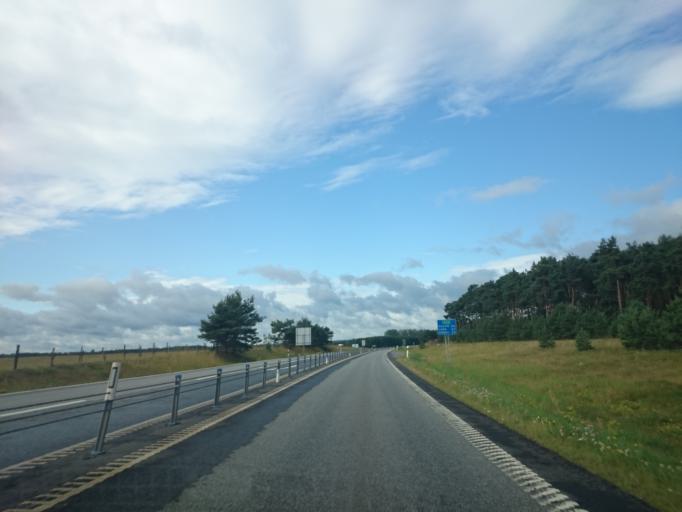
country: SE
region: Skane
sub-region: Kristianstads Kommun
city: Norra Asum
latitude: 55.9489
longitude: 14.0602
